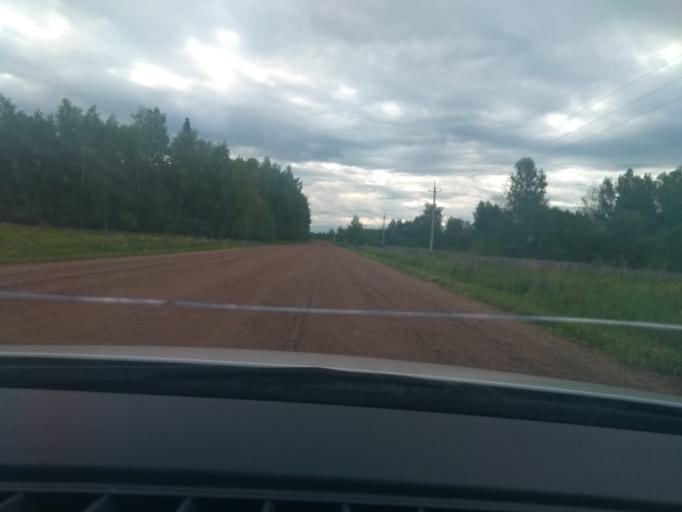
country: RU
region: Perm
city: Sylva
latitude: 57.8179
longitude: 56.7229
